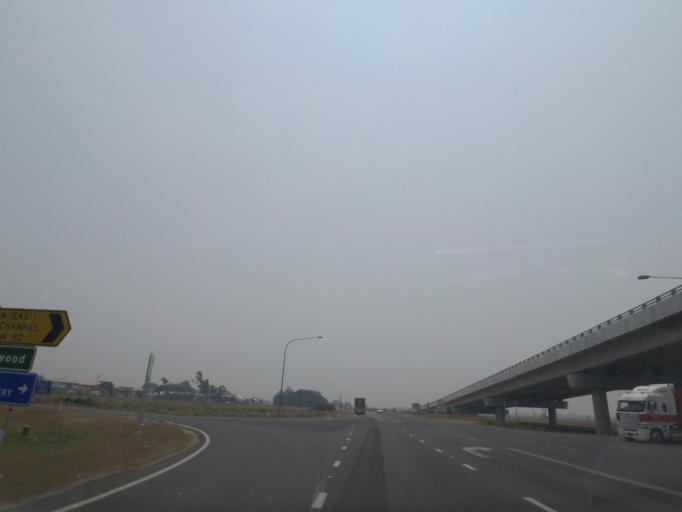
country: AU
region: New South Wales
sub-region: Clarence Valley
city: Maclean
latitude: -29.4253
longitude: 153.2411
